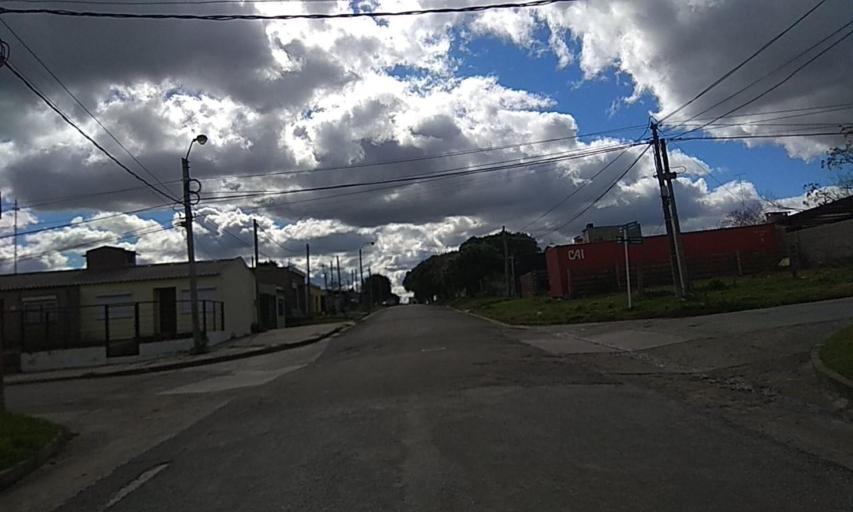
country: UY
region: Florida
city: Florida
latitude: -34.0903
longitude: -56.2303
